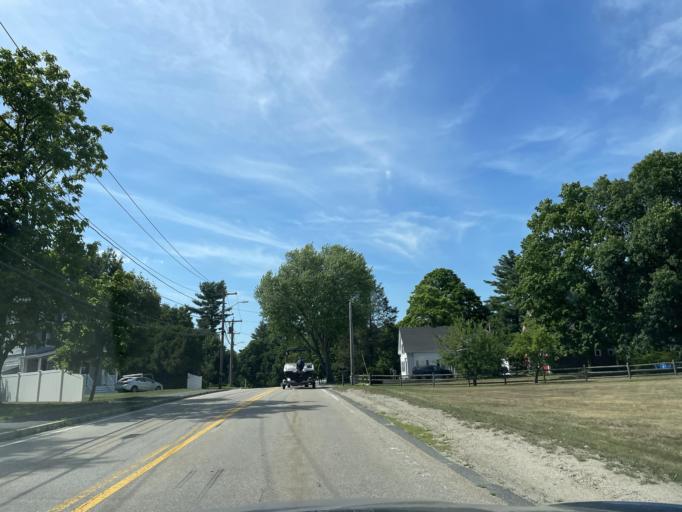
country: US
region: Massachusetts
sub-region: Norfolk County
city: Wrentham
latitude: 42.0737
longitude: -71.3305
